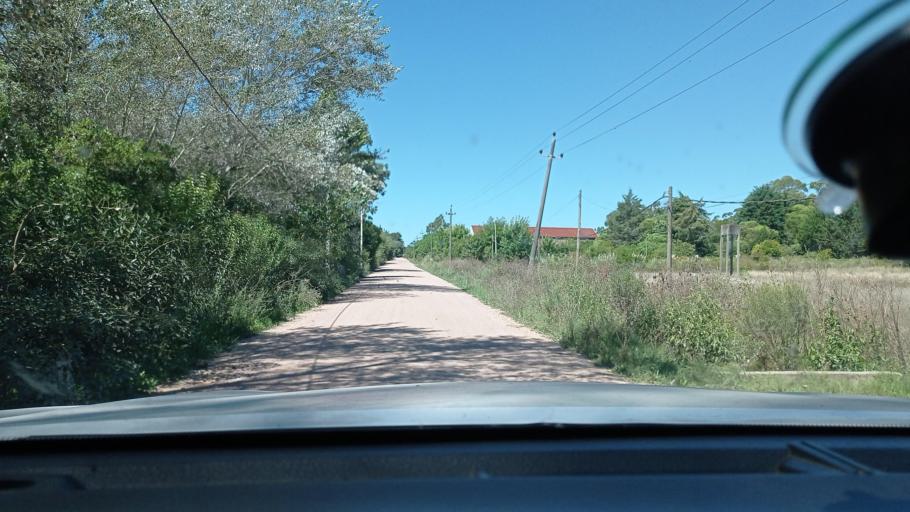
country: UY
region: Canelones
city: La Paz
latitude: -34.7597
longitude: -56.1699
